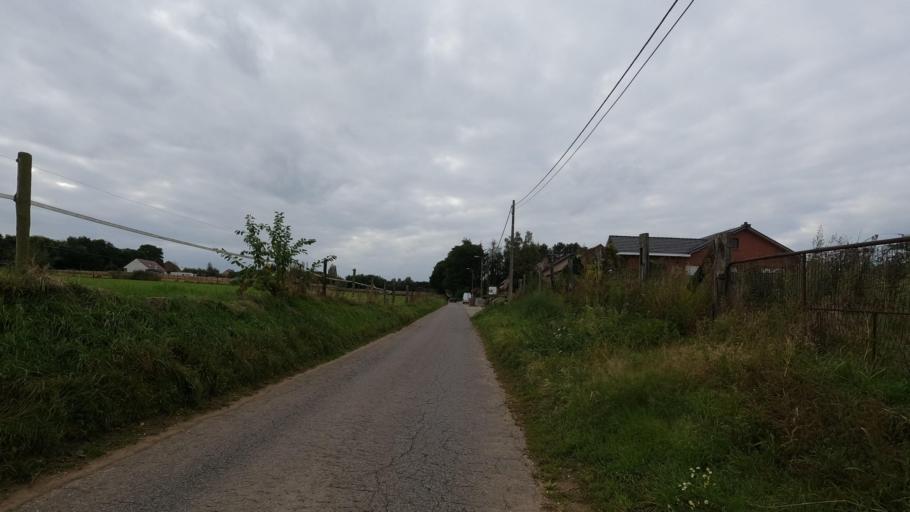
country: BE
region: Flanders
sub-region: Provincie Vlaams-Brabant
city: Aarschot
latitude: 50.9740
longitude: 4.8886
